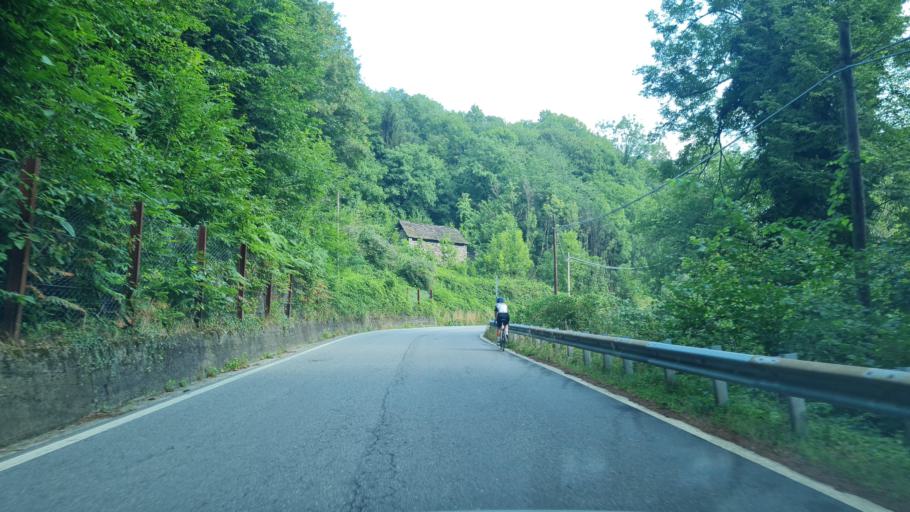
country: IT
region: Piedmont
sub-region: Provincia Verbano-Cusio-Ossola
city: Baceno
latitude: 46.2402
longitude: 8.3210
